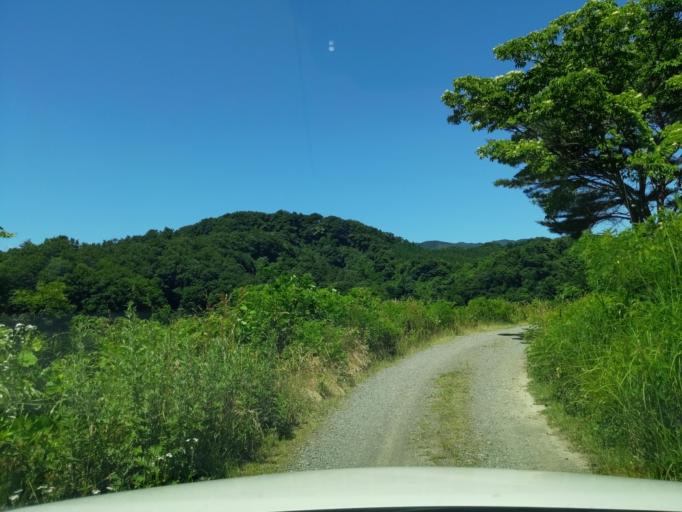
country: JP
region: Fukushima
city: Koriyama
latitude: 37.3859
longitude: 140.2538
